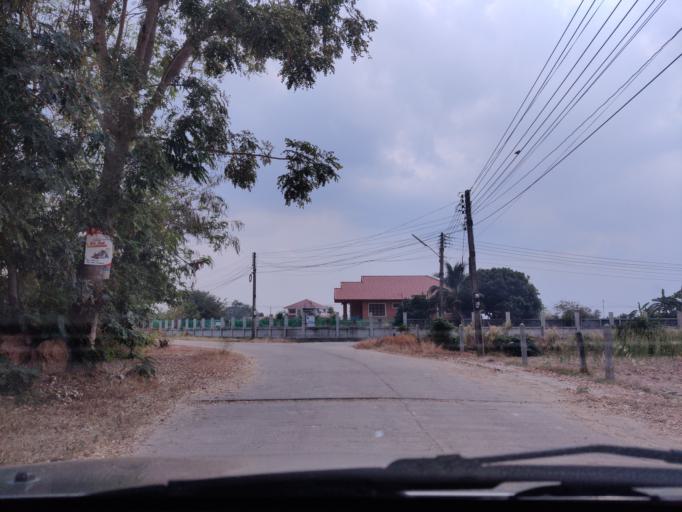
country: TH
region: Sisaket
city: Si Sa Ket
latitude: 15.1039
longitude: 104.3500
